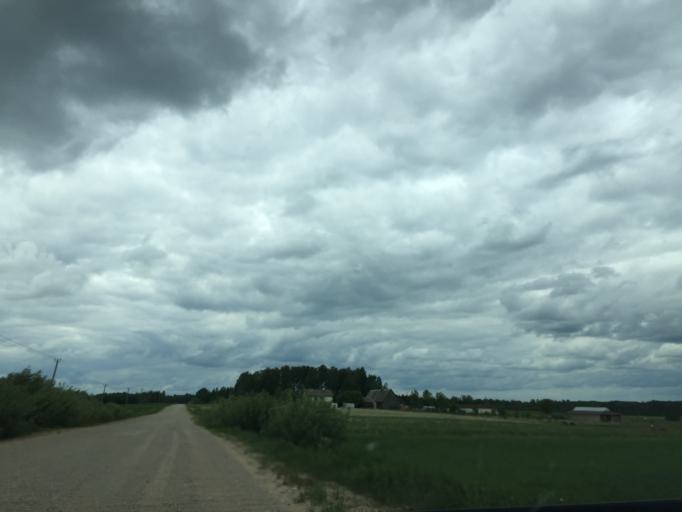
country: LV
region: Dagda
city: Dagda
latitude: 55.9800
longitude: 27.6059
